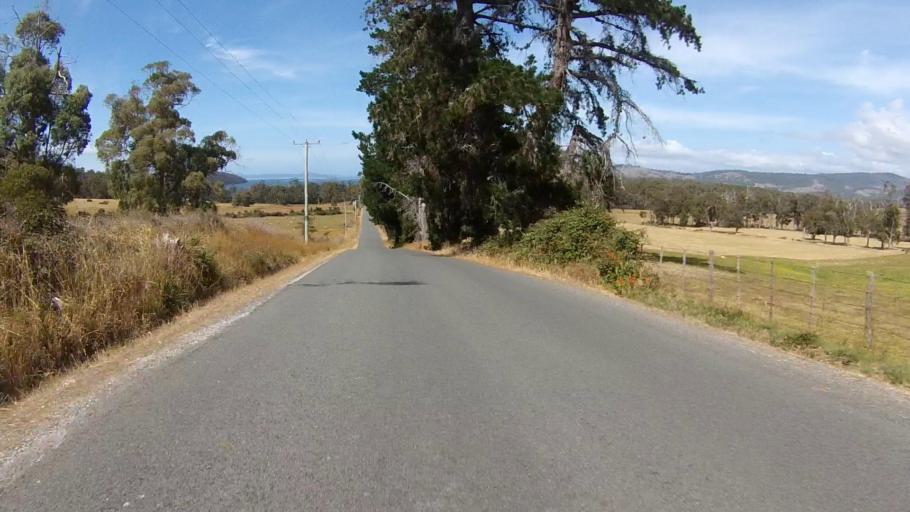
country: AU
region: Tasmania
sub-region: Huon Valley
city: Cygnet
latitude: -43.2351
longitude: 147.1256
